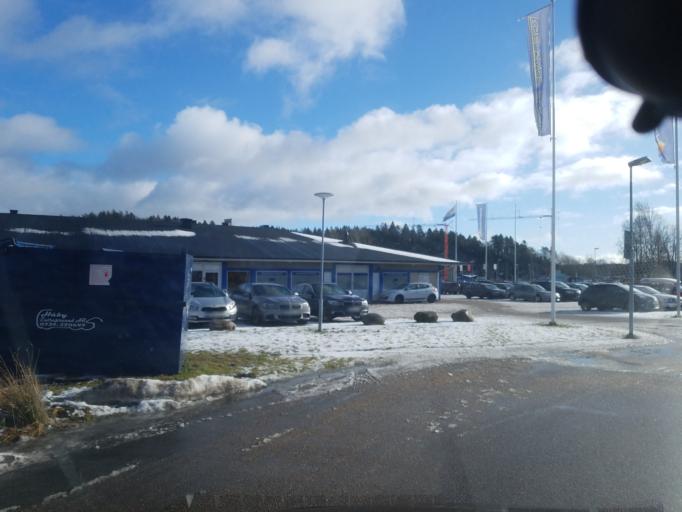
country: SE
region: Vaestra Goetaland
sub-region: Uddevalla Kommun
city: Uddevalla
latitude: 58.3510
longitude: 11.8460
